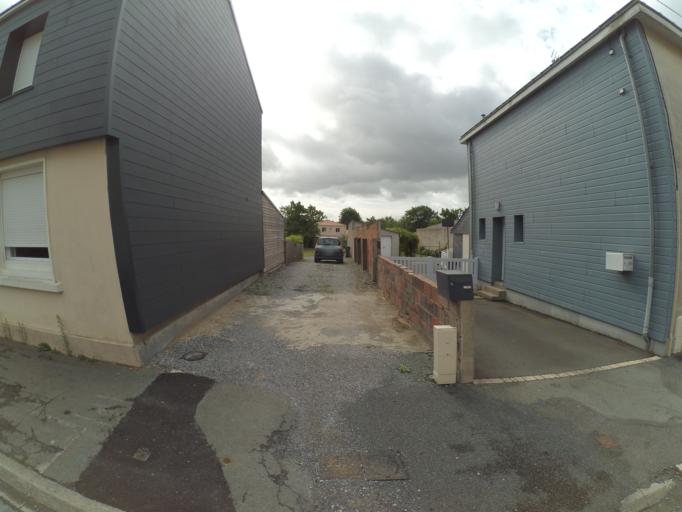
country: FR
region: Pays de la Loire
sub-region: Departement de Maine-et-Loire
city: Villedieu-la-Blouere
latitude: 47.1504
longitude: -1.0605
